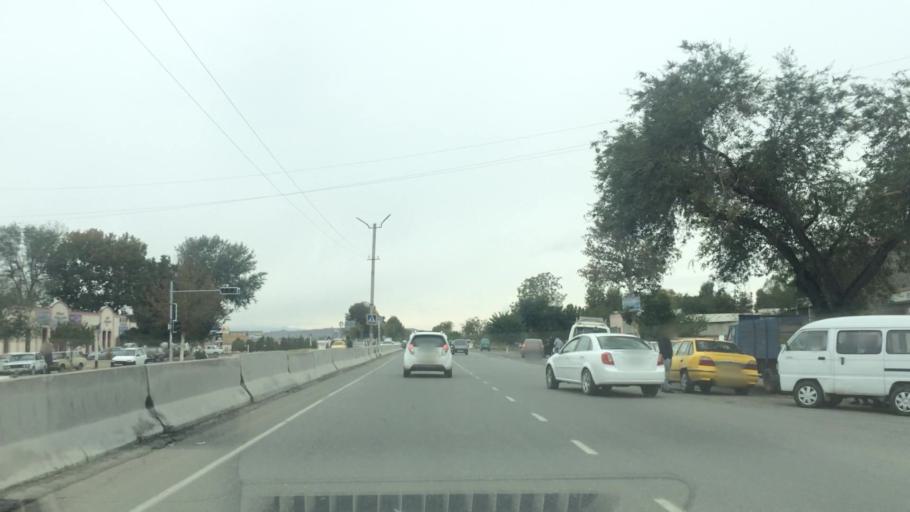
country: UZ
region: Samarqand
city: Jomboy
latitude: 39.7144
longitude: 67.1020
